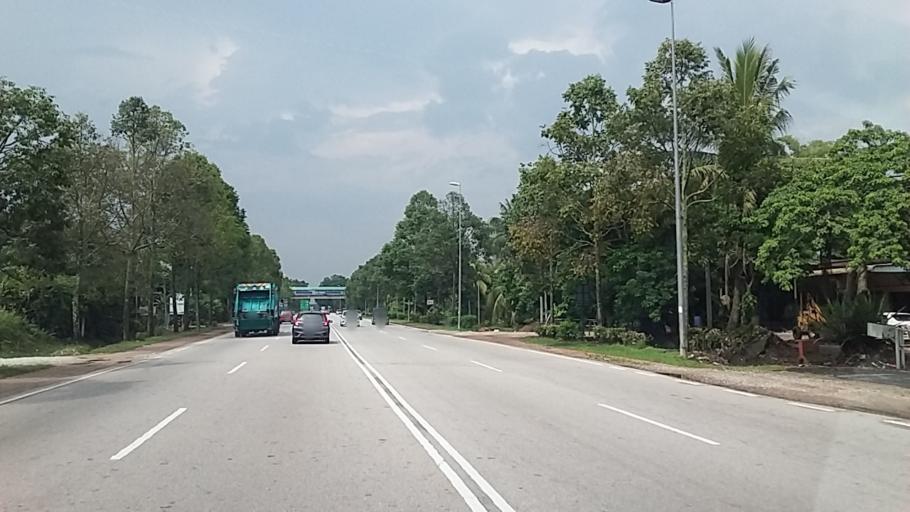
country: MY
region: Johor
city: Parit Raja
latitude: 1.8701
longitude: 103.1264
